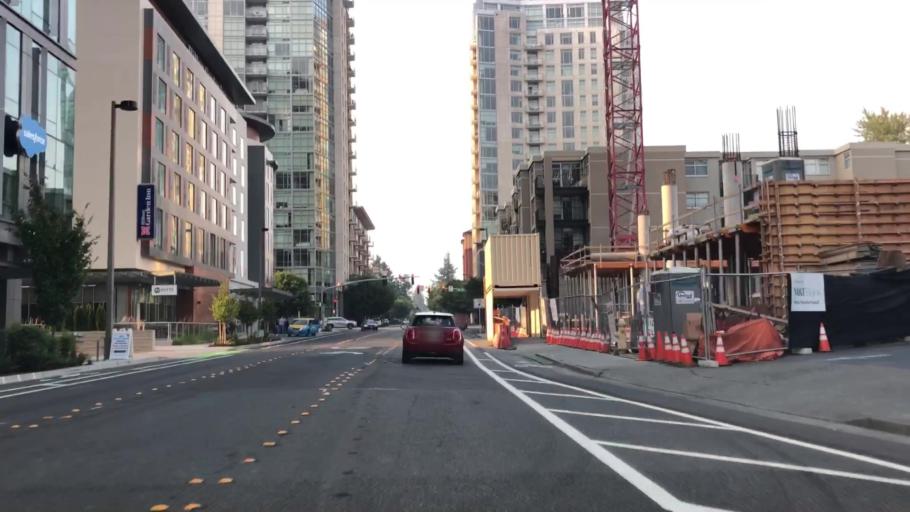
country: US
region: Washington
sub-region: King County
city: Bellevue
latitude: 47.6181
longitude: -122.1963
